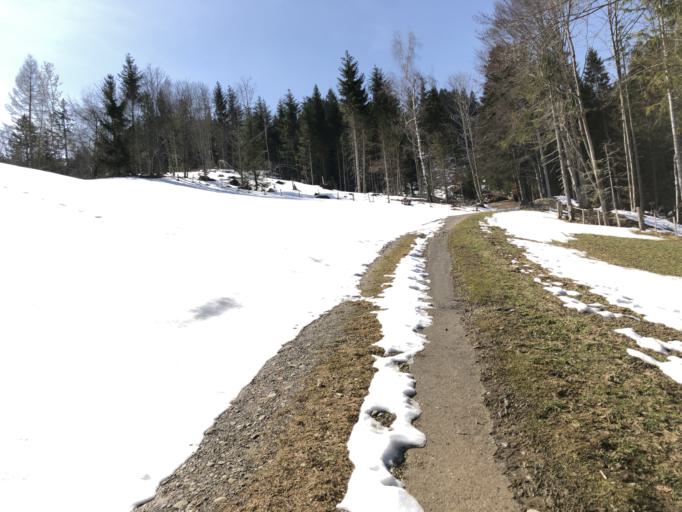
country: CH
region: Appenzell Innerrhoden
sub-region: Appenzell Inner Rhodes
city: Gonten
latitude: 47.3429
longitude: 9.3443
